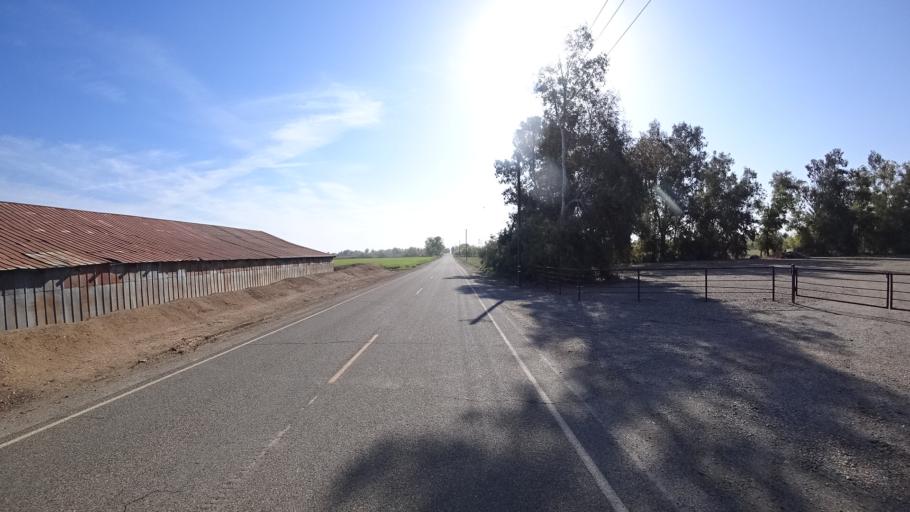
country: US
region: California
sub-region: Glenn County
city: Willows
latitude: 39.5388
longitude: -122.1809
